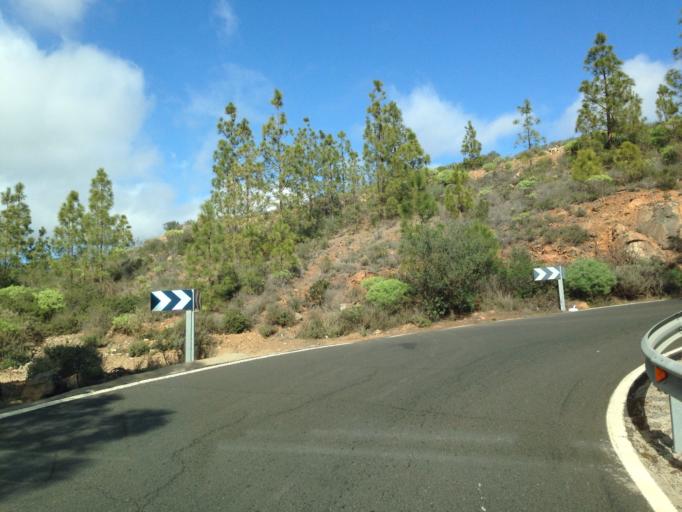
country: ES
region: Canary Islands
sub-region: Provincia de Las Palmas
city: San Bartolome
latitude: 27.9069
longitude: -15.5699
